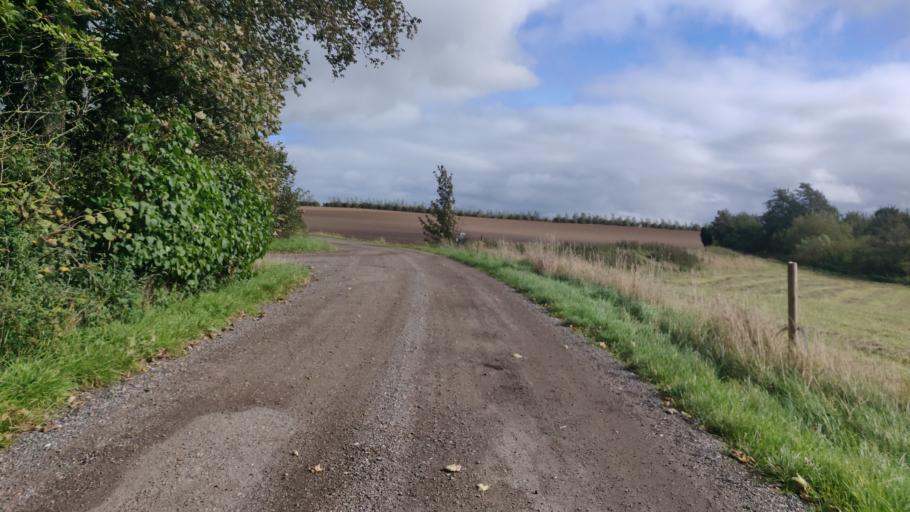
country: DK
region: South Denmark
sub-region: Kolding Kommune
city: Lunderskov
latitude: 55.5363
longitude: 9.3690
